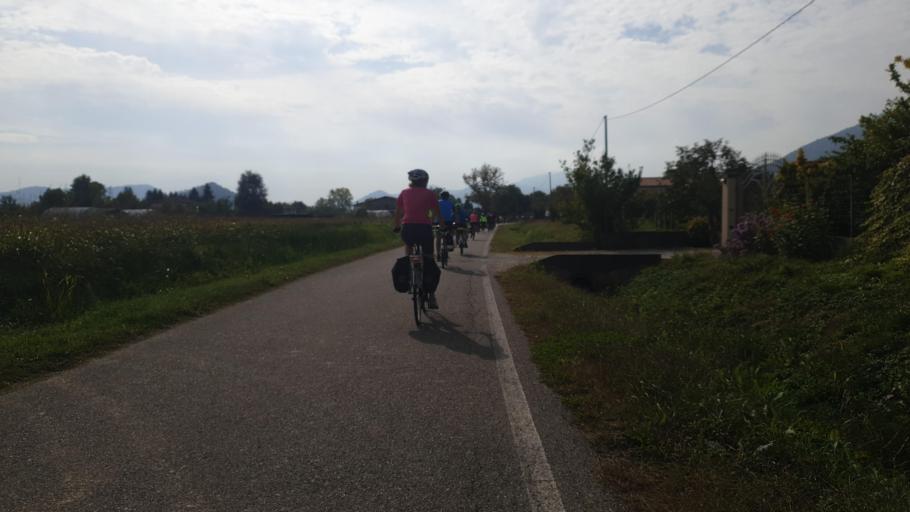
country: IT
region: Veneto
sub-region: Provincia di Padova
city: Montemerlo
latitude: 45.3934
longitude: 11.6915
